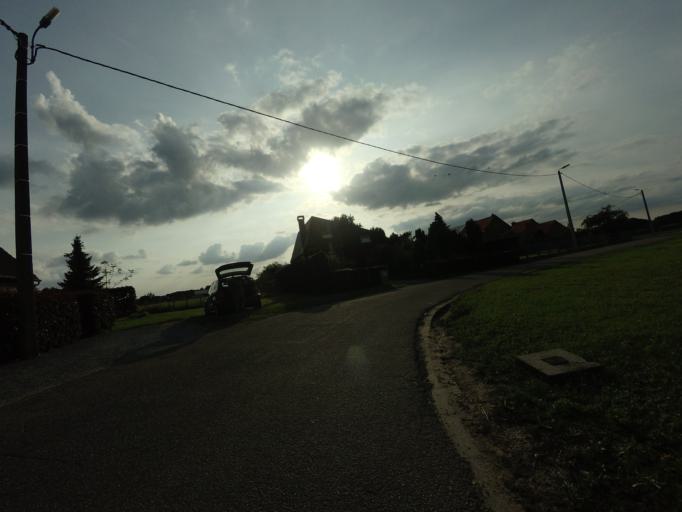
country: BE
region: Flanders
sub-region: Provincie Vlaams-Brabant
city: Kampenhout
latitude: 50.9245
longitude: 4.5603
